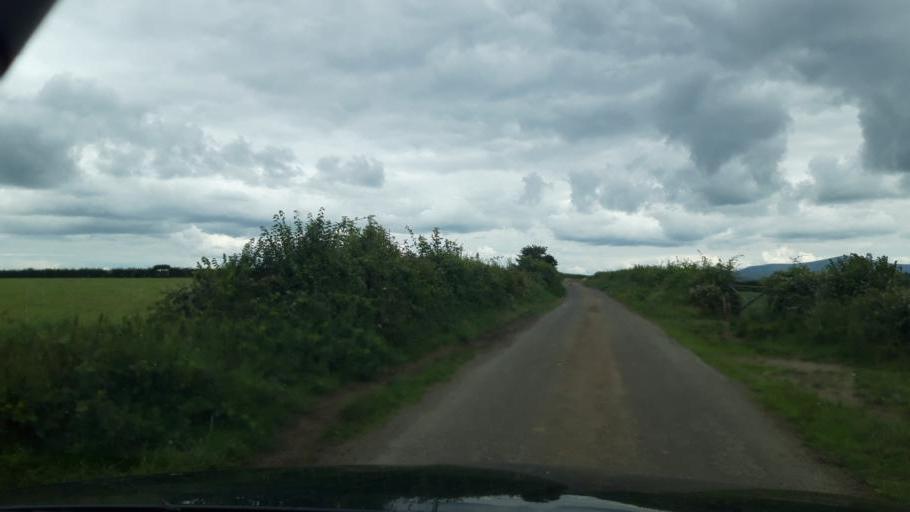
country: IE
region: Leinster
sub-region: Kilkenny
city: Graiguenamanagh
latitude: 52.6029
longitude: -7.0352
